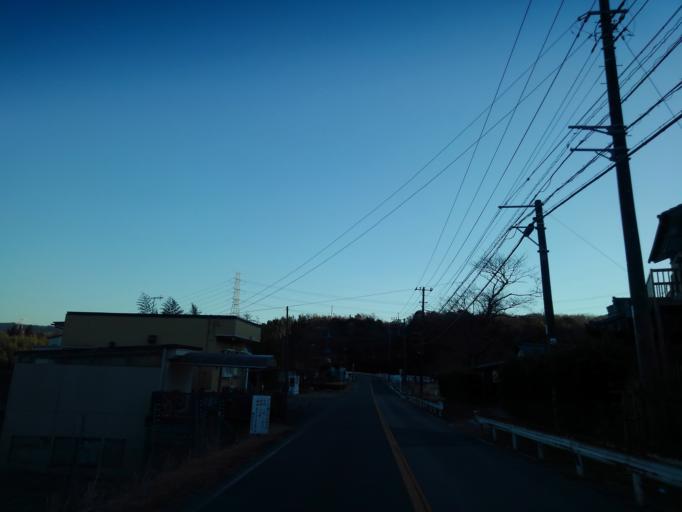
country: JP
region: Chiba
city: Kimitsu
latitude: 35.2909
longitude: 139.9776
